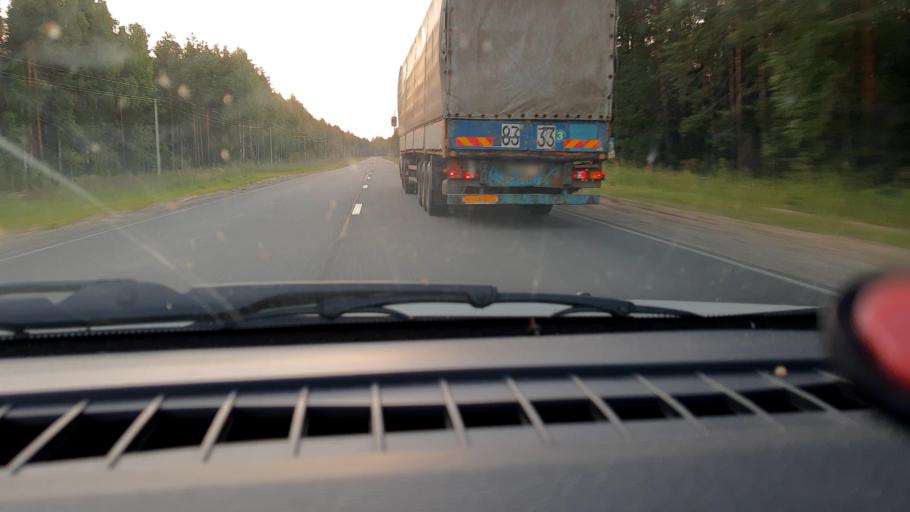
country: RU
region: Nizjnij Novgorod
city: Uren'
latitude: 57.3794
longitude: 45.6903
